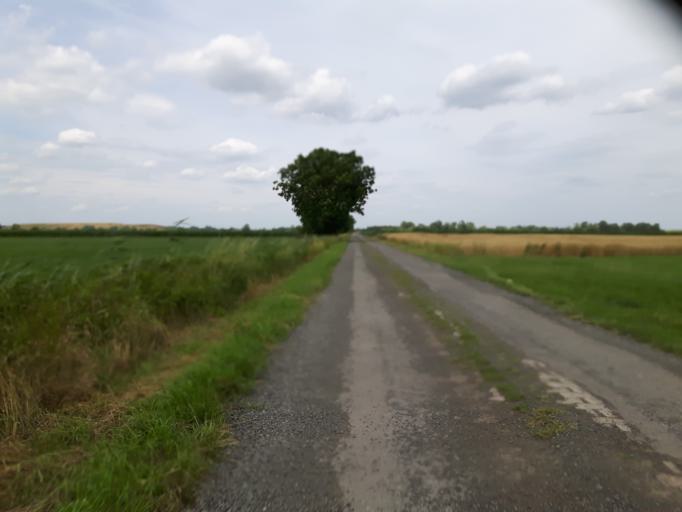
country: DE
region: Lower Saxony
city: Varel
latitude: 53.3915
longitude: 8.1963
